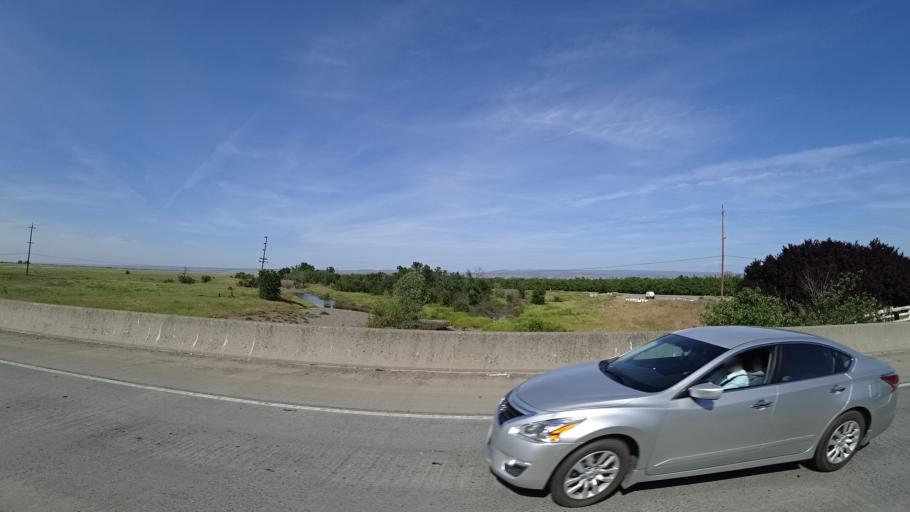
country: US
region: California
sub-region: Glenn County
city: Hamilton City
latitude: 39.8861
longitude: -121.9797
